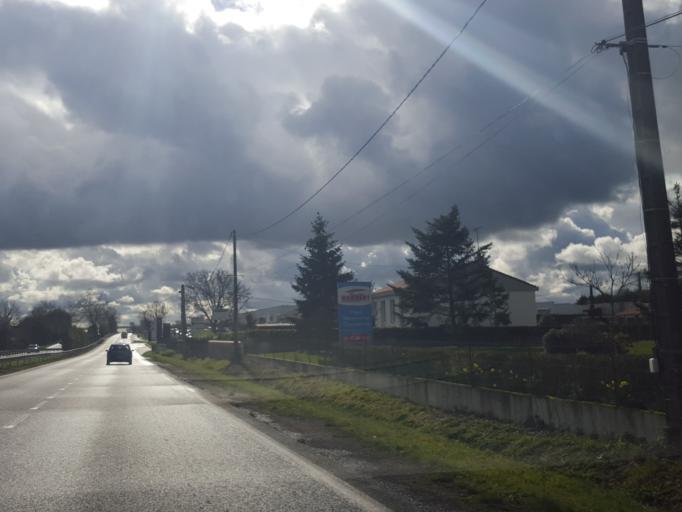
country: FR
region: Pays de la Loire
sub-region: Departement de la Vendee
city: Belleville-sur-Vie
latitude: 46.7518
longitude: -1.4306
